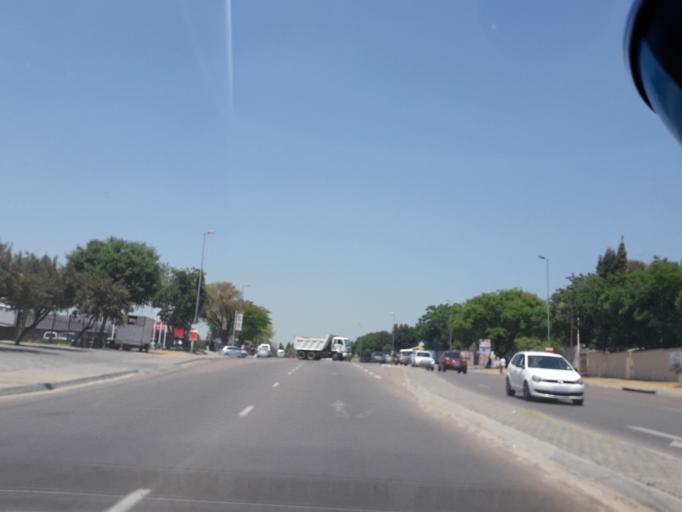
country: ZA
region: Gauteng
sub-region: City of Johannesburg Metropolitan Municipality
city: Midrand
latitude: -25.9508
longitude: 28.1235
